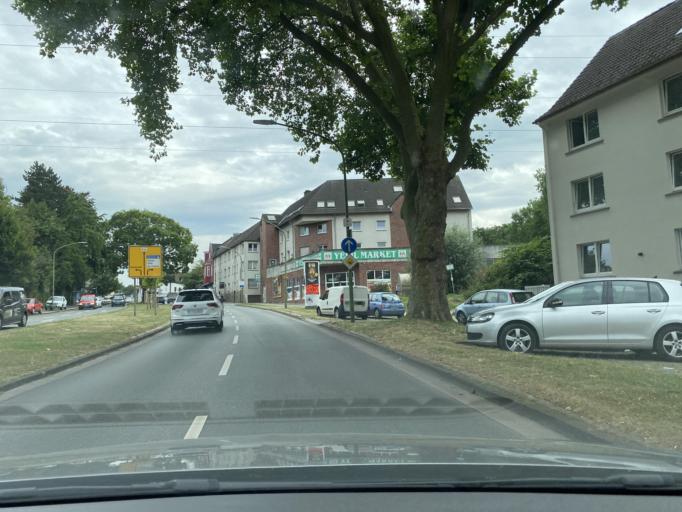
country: GB
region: England
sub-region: Essex
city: Frinton-on-Sea
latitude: 51.7516
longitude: 1.2862
